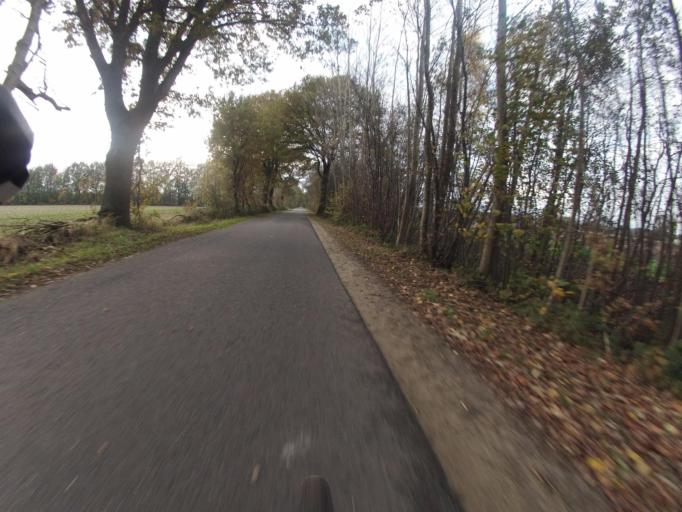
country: DE
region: North Rhine-Westphalia
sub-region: Regierungsbezirk Munster
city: Horstel
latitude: 52.2619
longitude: 7.5655
